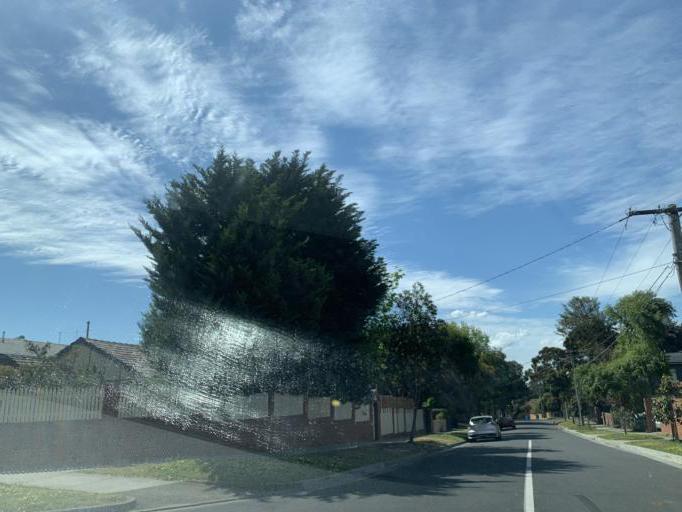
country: AU
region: Victoria
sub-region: Bayside
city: Hampton East
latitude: -37.9435
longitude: 145.0291
